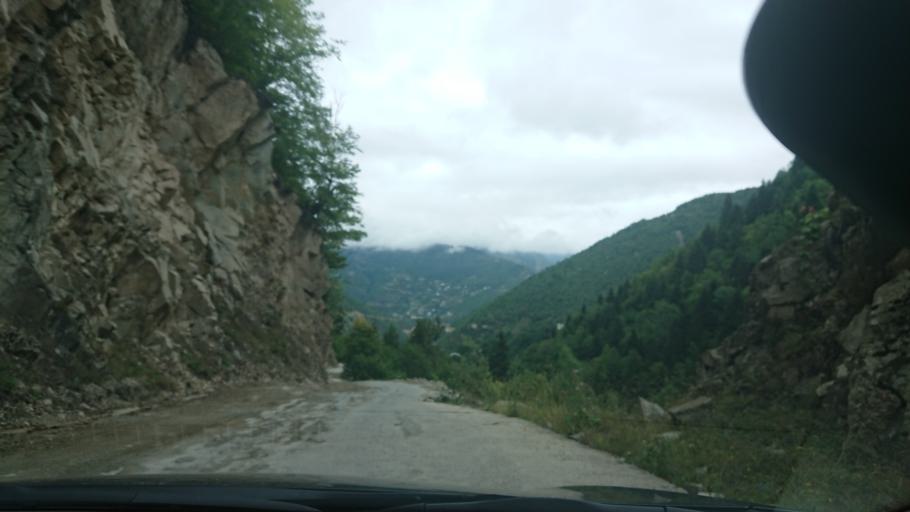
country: TR
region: Gumushane
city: Kurtun
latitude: 40.6813
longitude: 39.0495
